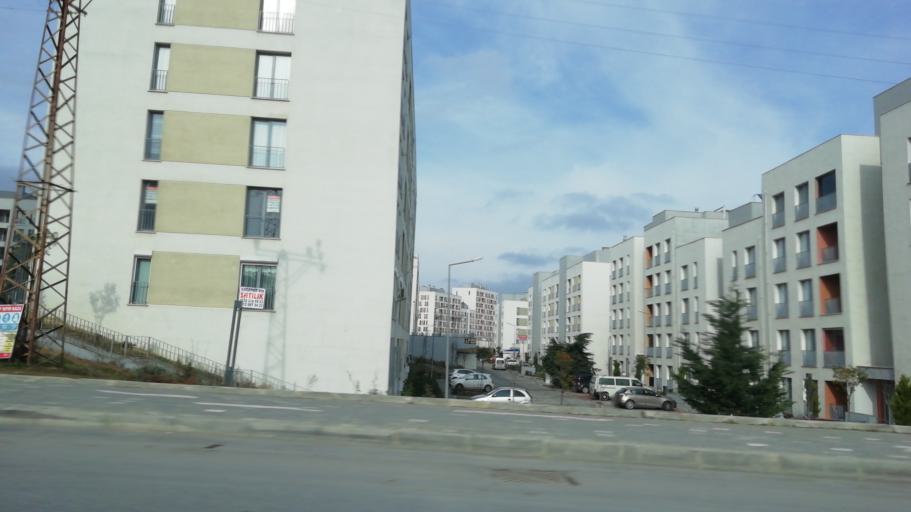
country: TR
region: Istanbul
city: Basaksehir
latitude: 41.1306
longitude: 28.7821
